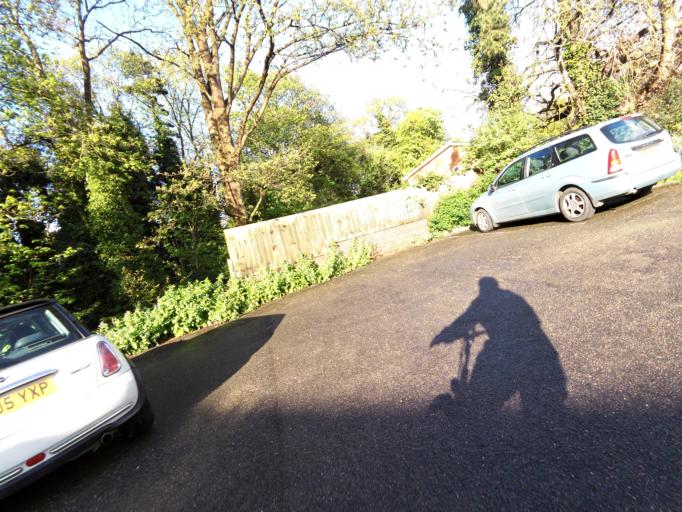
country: GB
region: England
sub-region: Suffolk
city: Ipswich
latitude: 52.0507
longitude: 1.1721
